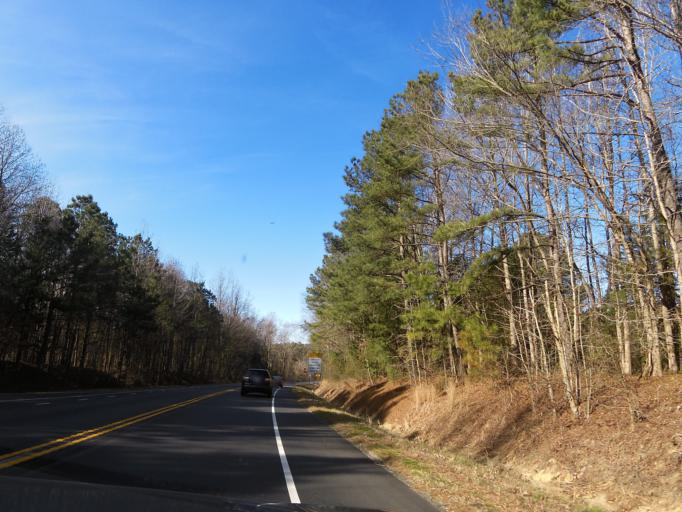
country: US
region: Virginia
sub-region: Isle of Wight County
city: Smithfield
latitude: 36.9727
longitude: -76.6370
